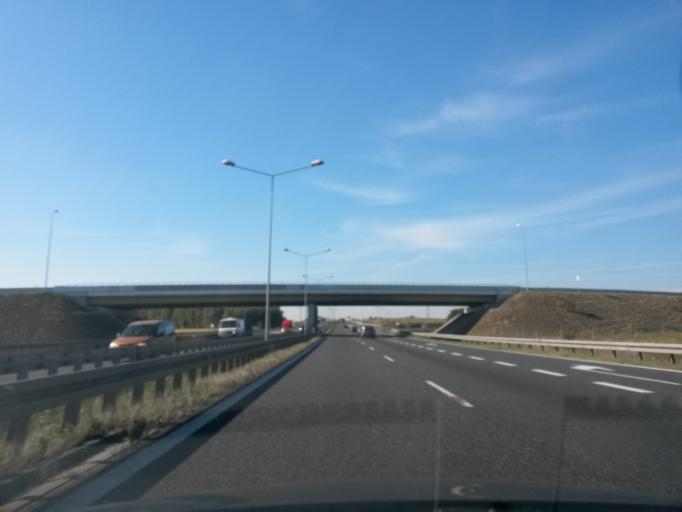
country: PL
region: Silesian Voivodeship
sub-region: Powiat gliwicki
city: Rudziniec
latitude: 50.3917
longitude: 18.4495
